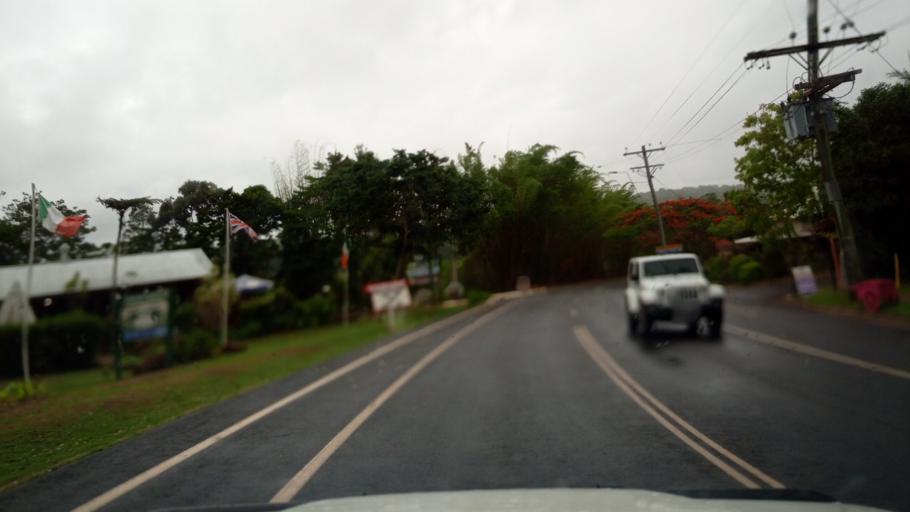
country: AU
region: Queensland
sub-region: Tablelands
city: Tolga
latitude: -17.2736
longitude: 145.5821
